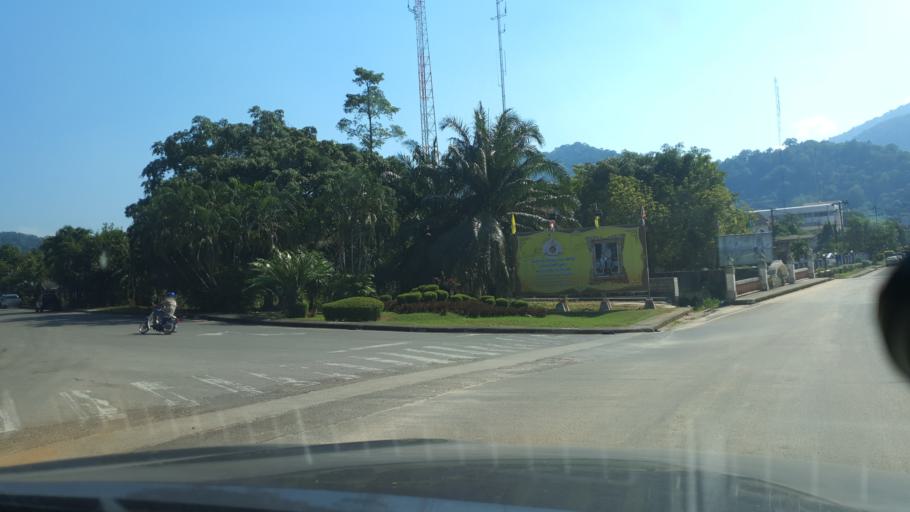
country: TH
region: Ranong
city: Ranong
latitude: 9.9651
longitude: 98.6396
